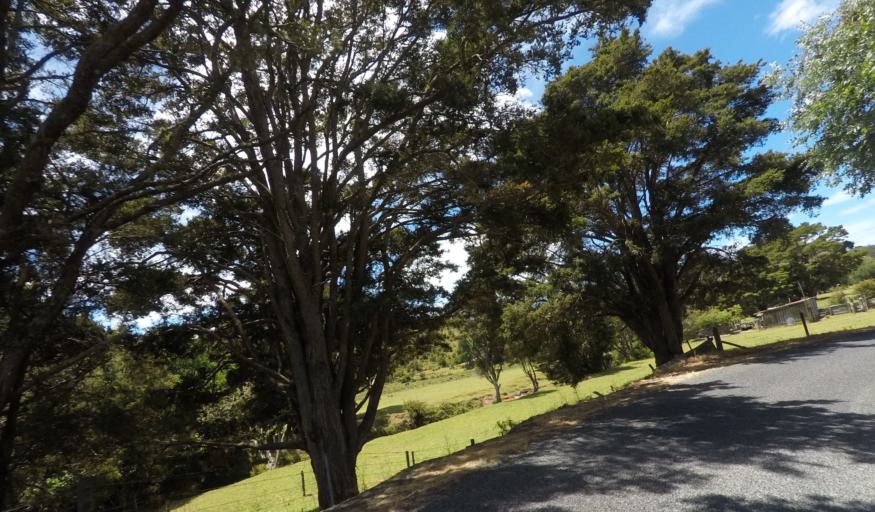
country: NZ
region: Northland
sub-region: Whangarei
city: Ngunguru
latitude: -35.5051
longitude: 174.4100
